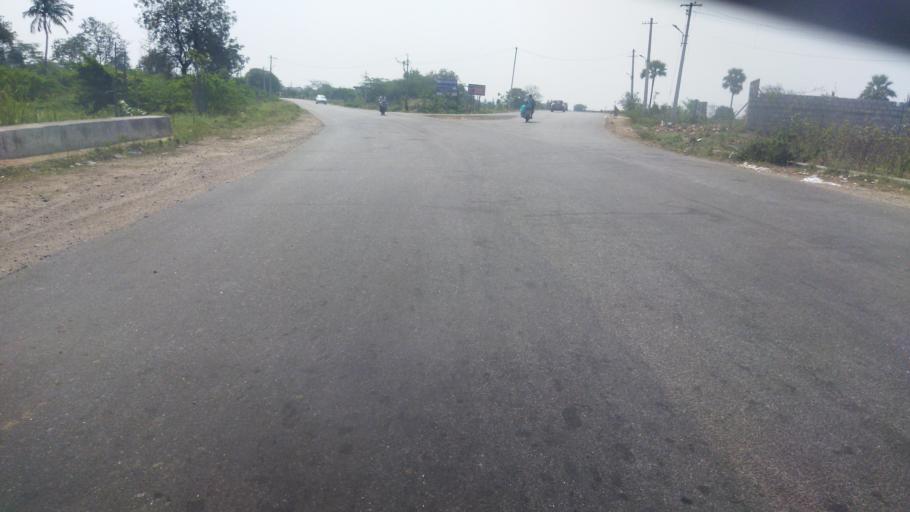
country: IN
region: Telangana
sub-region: Nalgonda
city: Nalgonda
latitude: 17.0842
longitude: 79.2844
